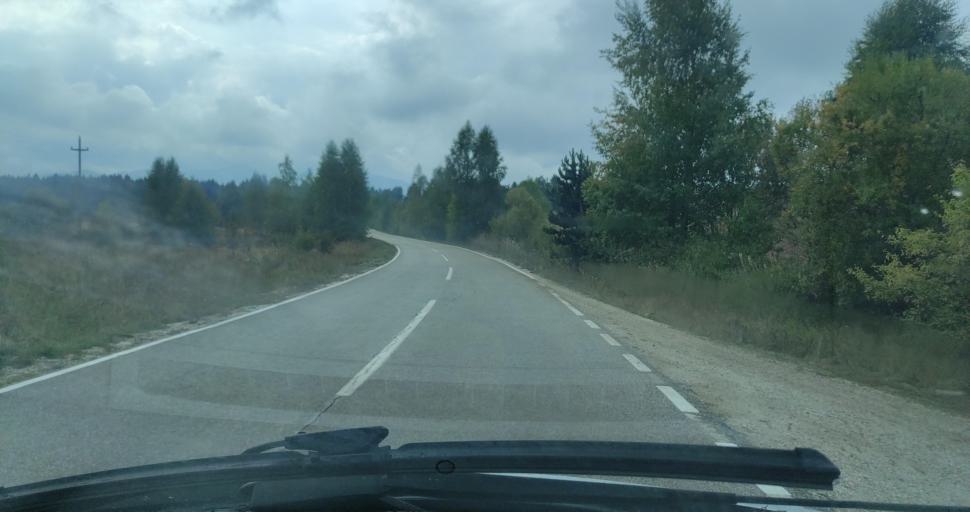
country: RS
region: Central Serbia
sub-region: Jablanicki Okrug
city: Crna Trava
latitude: 42.6947
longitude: 22.3217
